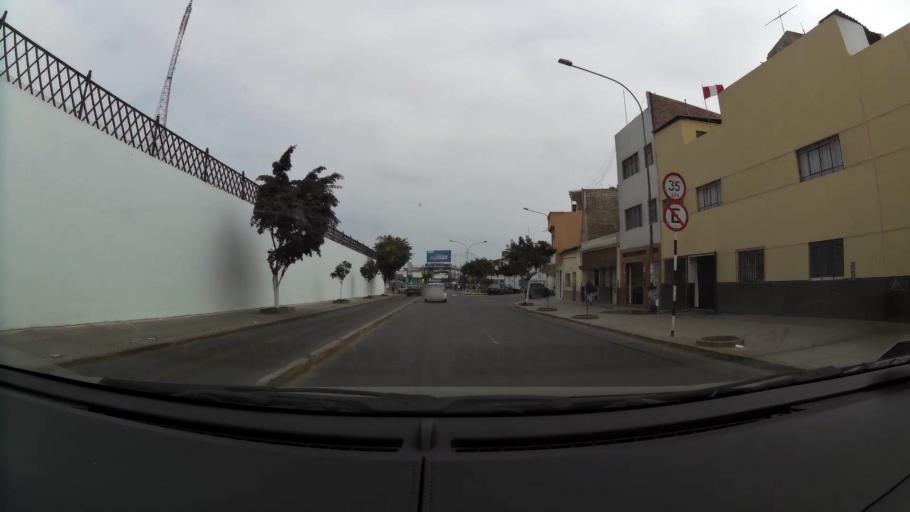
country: PE
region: La Libertad
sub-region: Provincia de Trujillo
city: Trujillo
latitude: -8.1101
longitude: -79.0219
